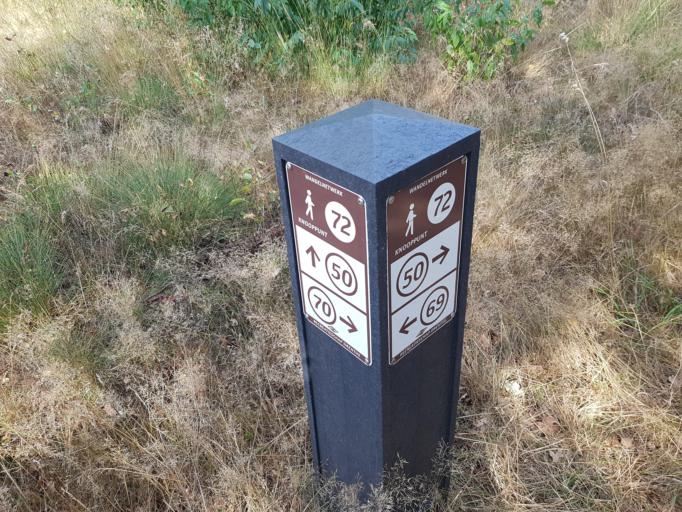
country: NL
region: Drenthe
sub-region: Gemeente Westerveld
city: Dwingeloo
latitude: 52.7991
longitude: 6.3608
